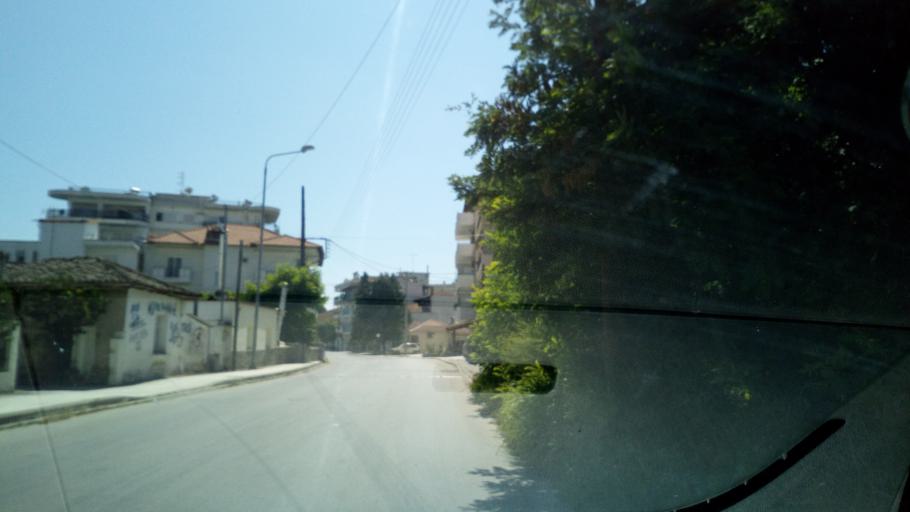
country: GR
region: Central Macedonia
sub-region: Nomos Thessalonikis
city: Lagkadas
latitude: 40.7531
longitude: 23.0693
